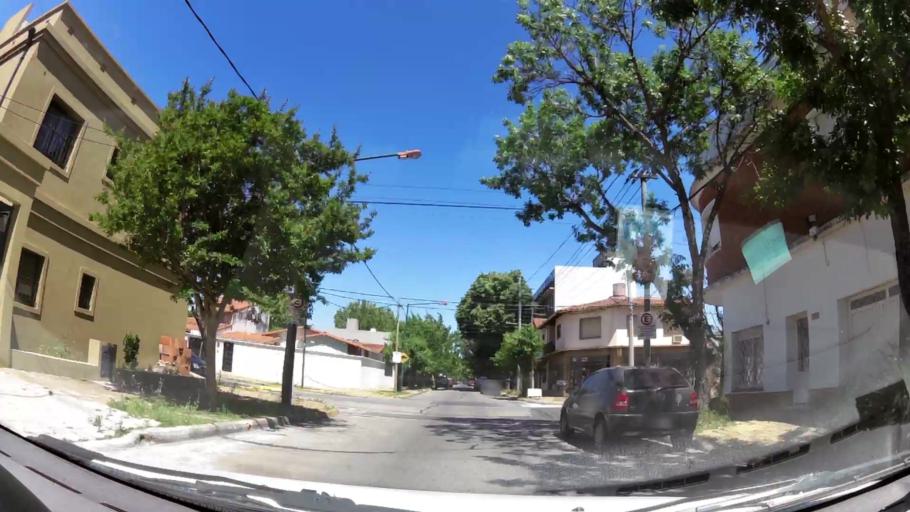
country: AR
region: Buenos Aires
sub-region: Partido de San Isidro
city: San Isidro
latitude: -34.4857
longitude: -58.5109
